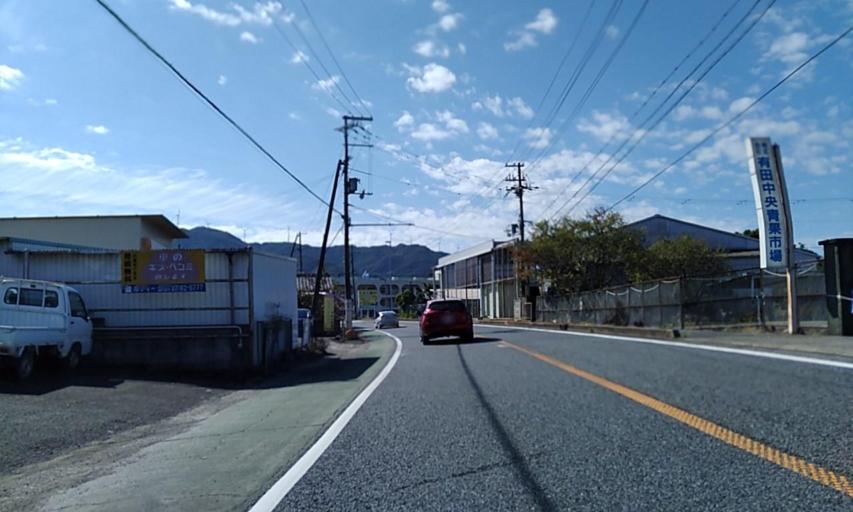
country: JP
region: Wakayama
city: Kainan
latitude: 34.0229
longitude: 135.1795
